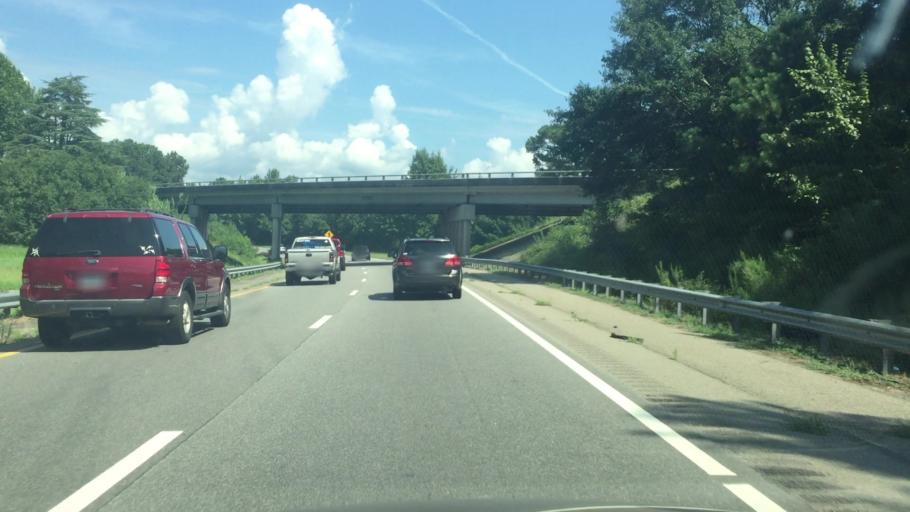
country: US
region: North Carolina
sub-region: Scotland County
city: Laurinburg
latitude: 34.7867
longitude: -79.5040
